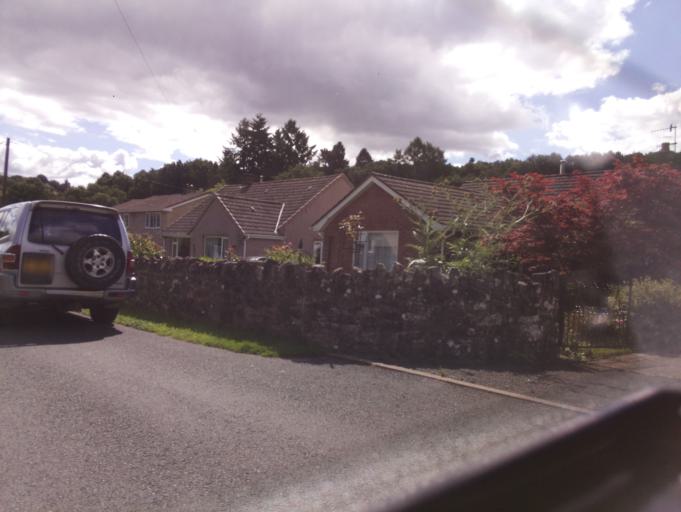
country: GB
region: England
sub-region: Gloucestershire
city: Cinderford
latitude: 51.7908
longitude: -2.5003
